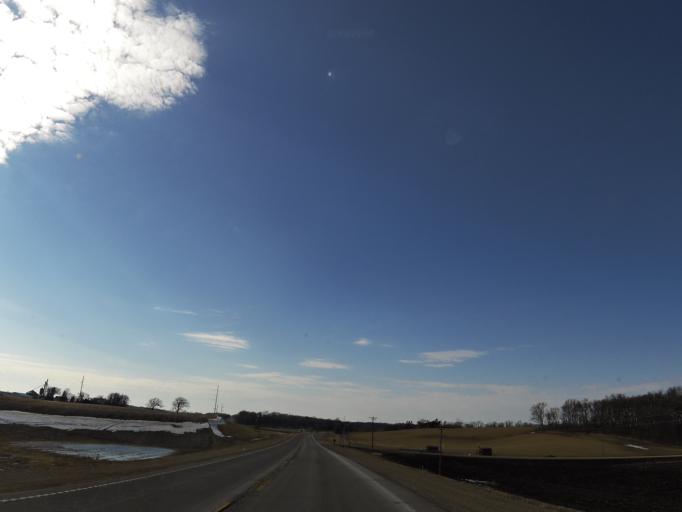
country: US
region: Minnesota
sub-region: Le Sueur County
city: Waterville
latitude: 44.1962
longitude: -93.5221
